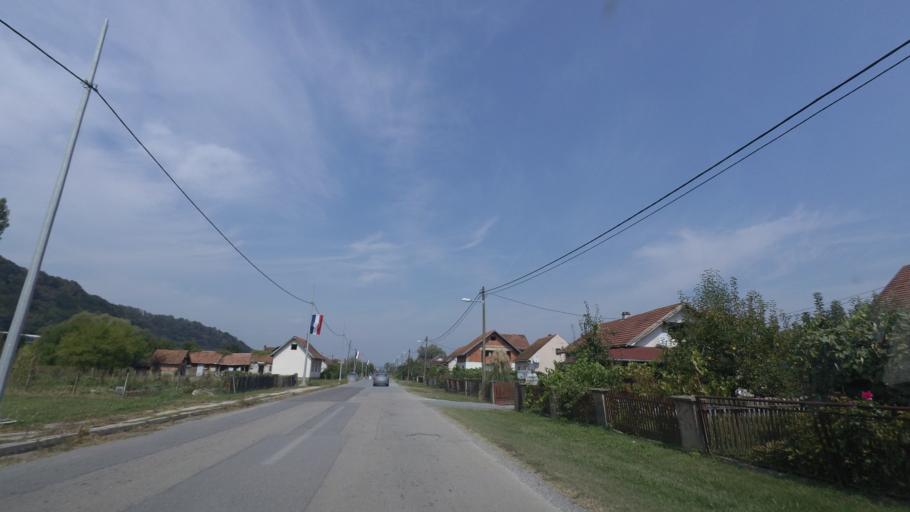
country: HR
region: Sisacko-Moslavacka
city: Glina
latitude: 45.3212
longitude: 16.1085
